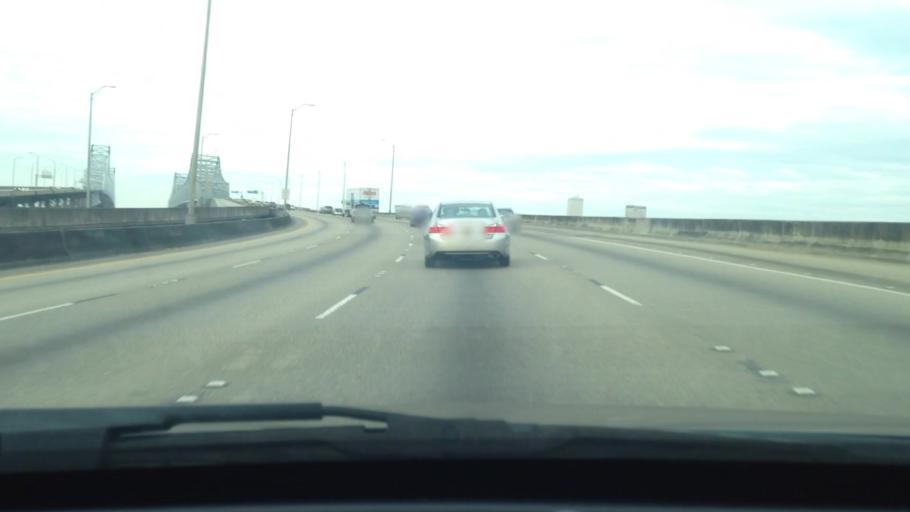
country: US
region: Louisiana
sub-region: Jefferson Parish
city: Gretna
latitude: 29.9382
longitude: -90.0410
